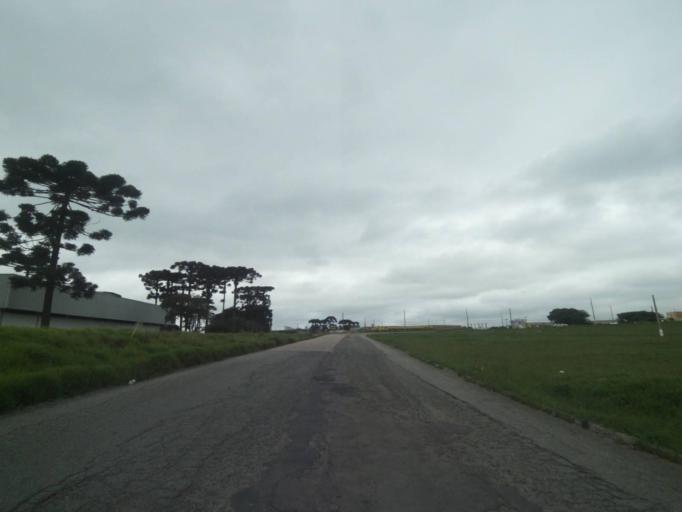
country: BR
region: Parana
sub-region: Araucaria
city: Araucaria
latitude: -25.5212
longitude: -49.3327
